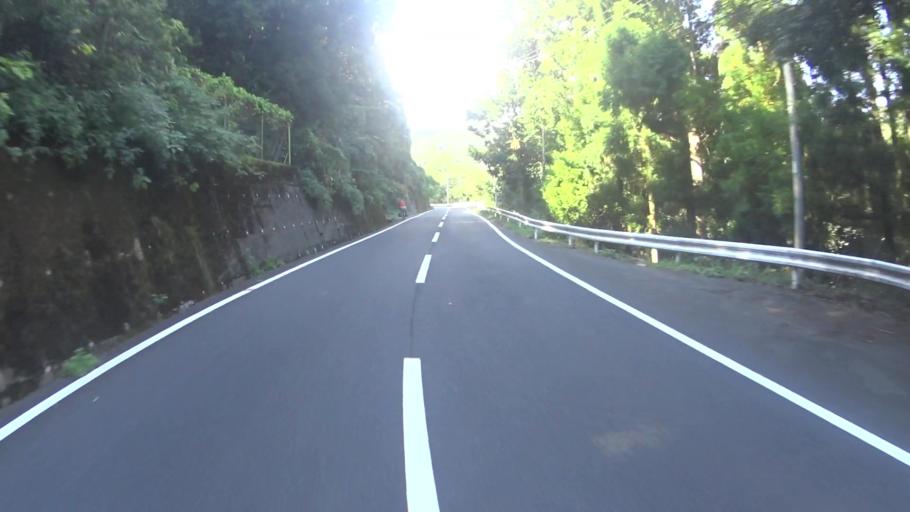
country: JP
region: Kyoto
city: Miyazu
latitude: 35.7051
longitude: 135.2821
